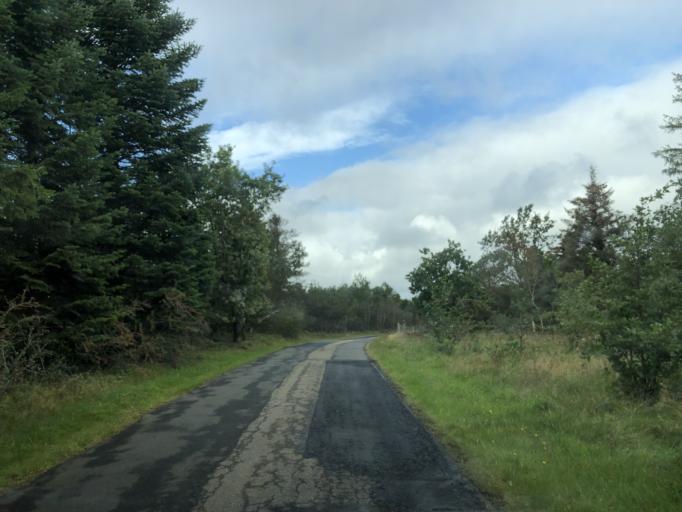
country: DK
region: Central Jutland
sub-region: Holstebro Kommune
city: Ulfborg
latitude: 56.3090
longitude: 8.4289
